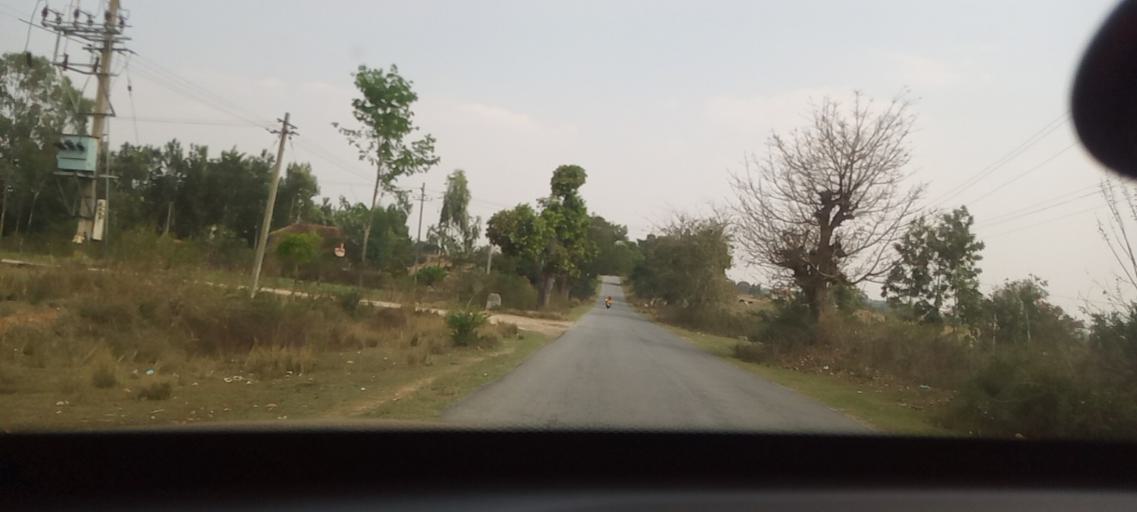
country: IN
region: Karnataka
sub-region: Hassan
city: Belur
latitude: 13.1796
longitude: 75.8443
